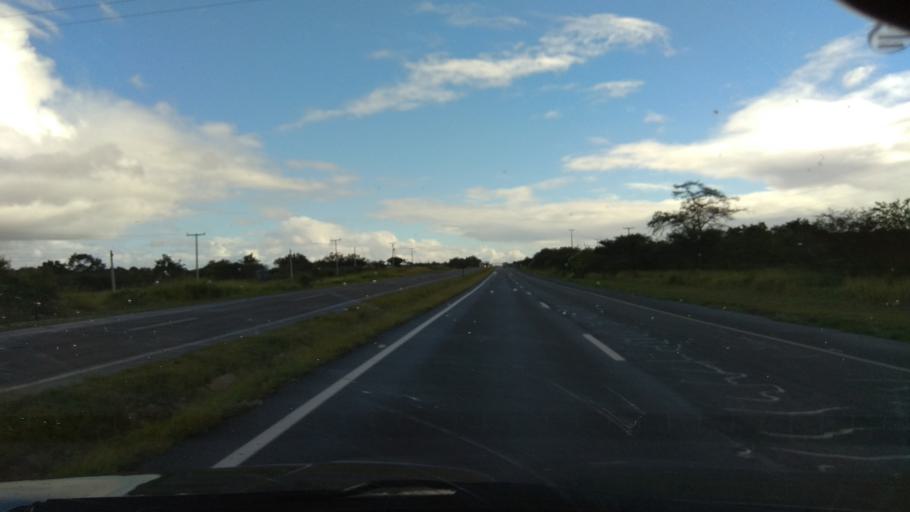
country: BR
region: Bahia
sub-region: Santo Estevao
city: Santo Estevao
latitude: -12.4866
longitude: -39.3235
